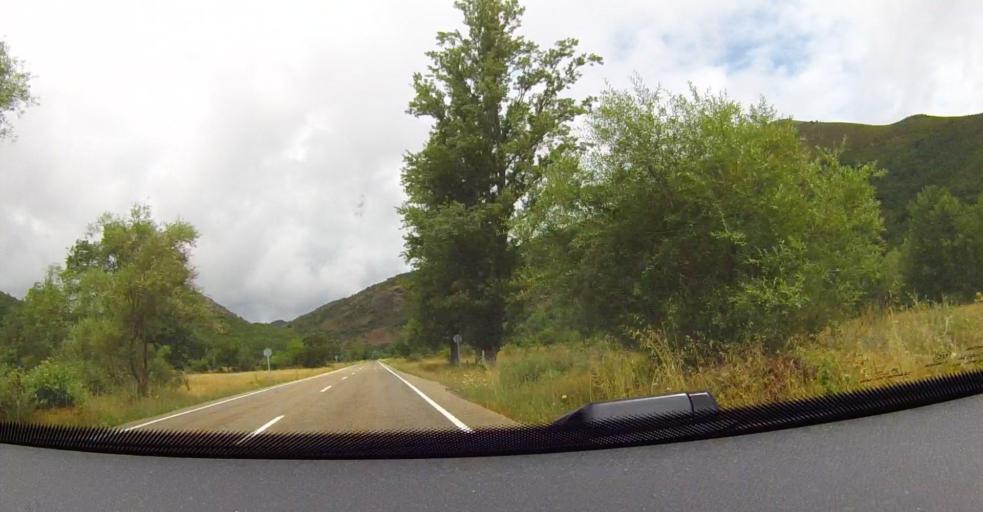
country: ES
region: Castille and Leon
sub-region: Provincia de Leon
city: Bonar
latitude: 42.8889
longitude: -5.3082
